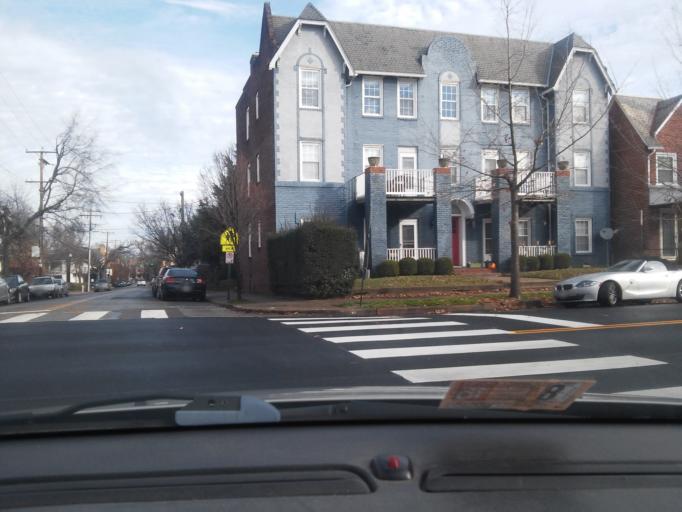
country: US
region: Virginia
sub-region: City of Richmond
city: Richmond
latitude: 37.5585
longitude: -77.4769
